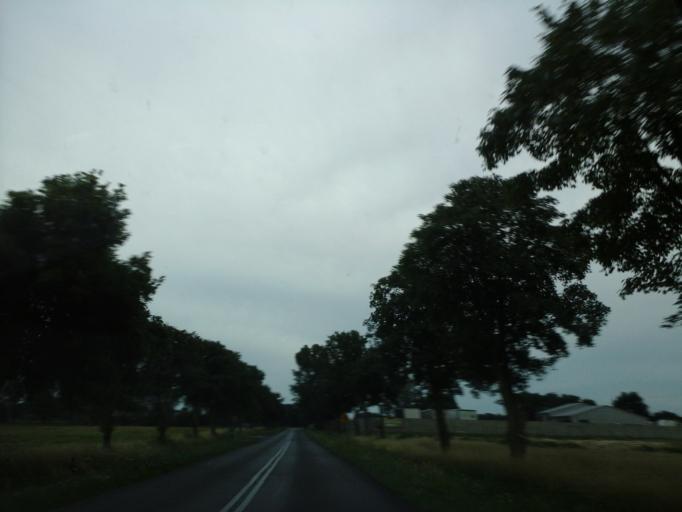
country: PL
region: West Pomeranian Voivodeship
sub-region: Powiat goleniowski
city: Nowogard
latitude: 53.6102
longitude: 15.1550
